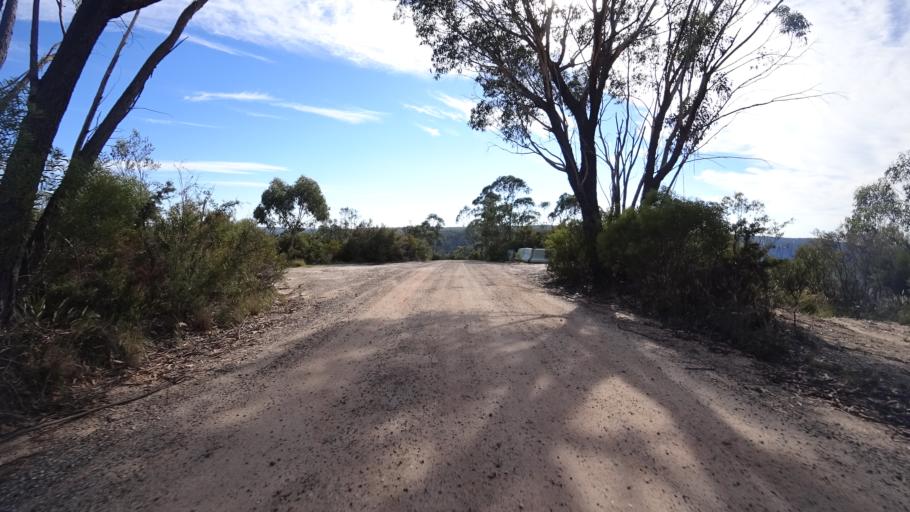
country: AU
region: New South Wales
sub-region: Lithgow
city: Lithgow
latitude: -33.5033
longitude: 150.1666
